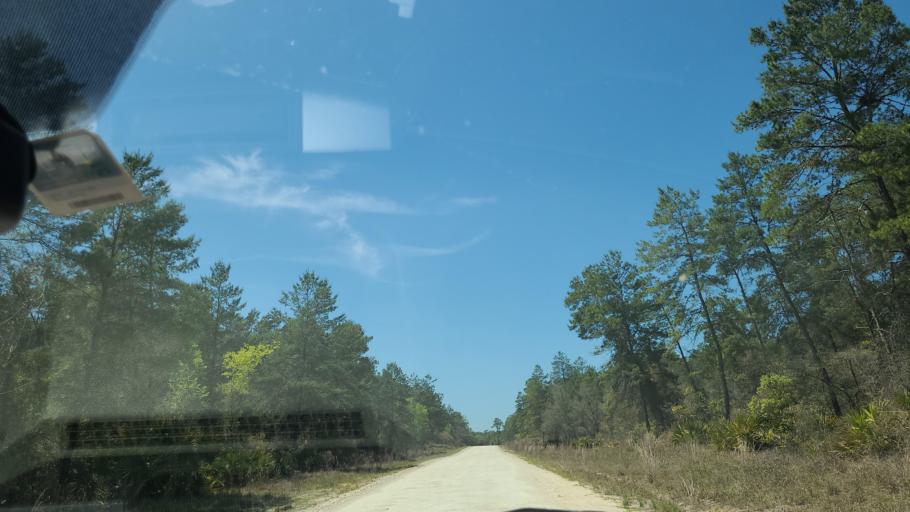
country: US
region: Florida
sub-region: Putnam County
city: Interlachen
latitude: 29.4331
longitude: -81.7509
